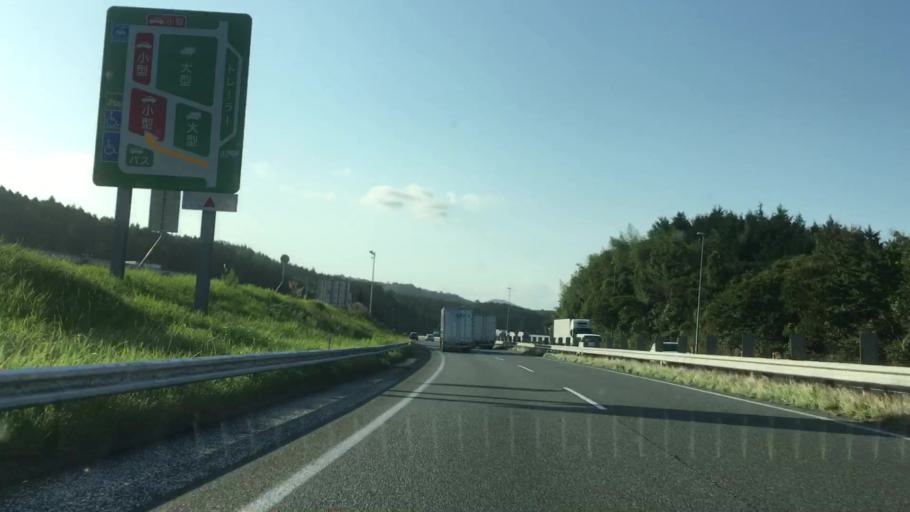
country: JP
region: Yamaguchi
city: Ogori-shimogo
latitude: 34.1525
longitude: 131.3398
